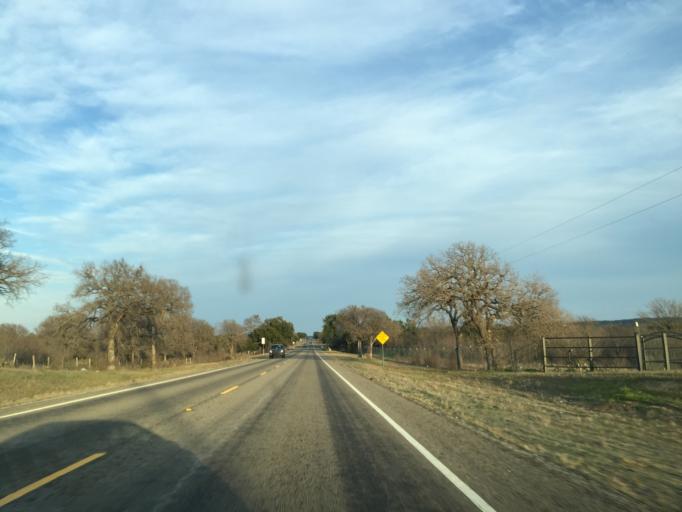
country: US
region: Texas
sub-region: Llano County
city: Buchanan Dam
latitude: 30.7328
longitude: -98.4895
